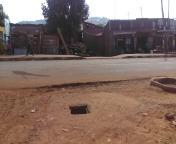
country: UG
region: Central Region
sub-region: Kampala District
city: Kampala
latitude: 0.2536
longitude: 32.5700
